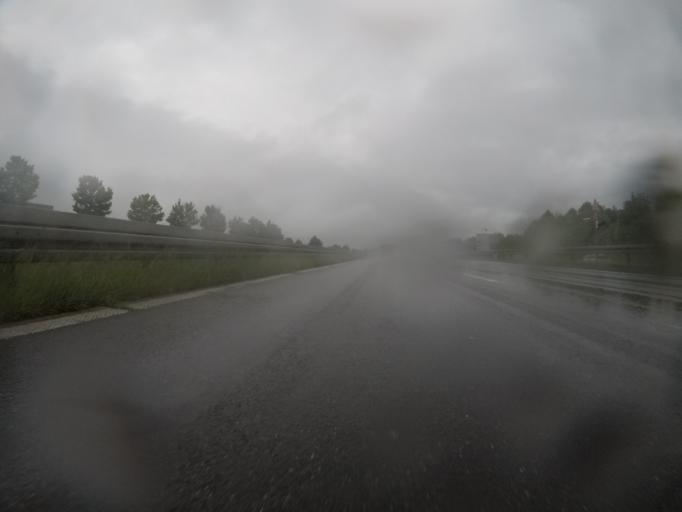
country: DE
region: Baden-Wuerttemberg
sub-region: Regierungsbezirk Stuttgart
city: Leinfelden-Echterdingen
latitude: 48.7243
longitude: 9.1647
